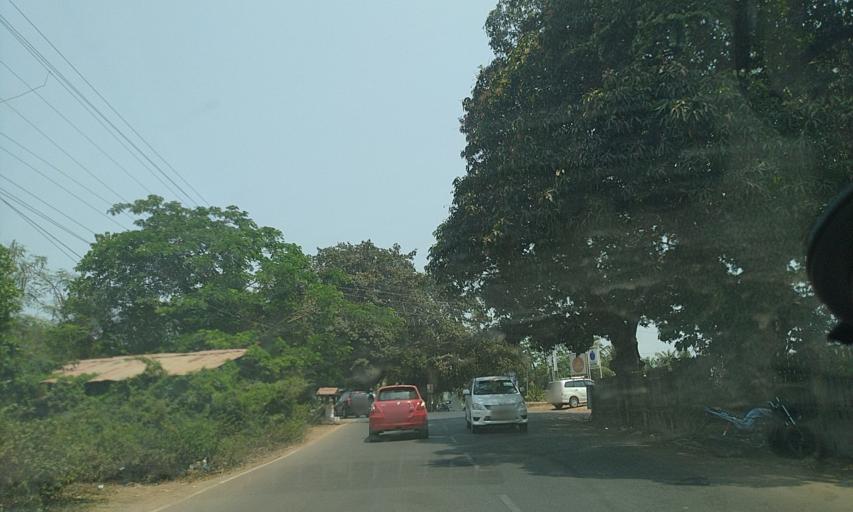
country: IN
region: Goa
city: Calangute
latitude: 15.5476
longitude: 73.7709
